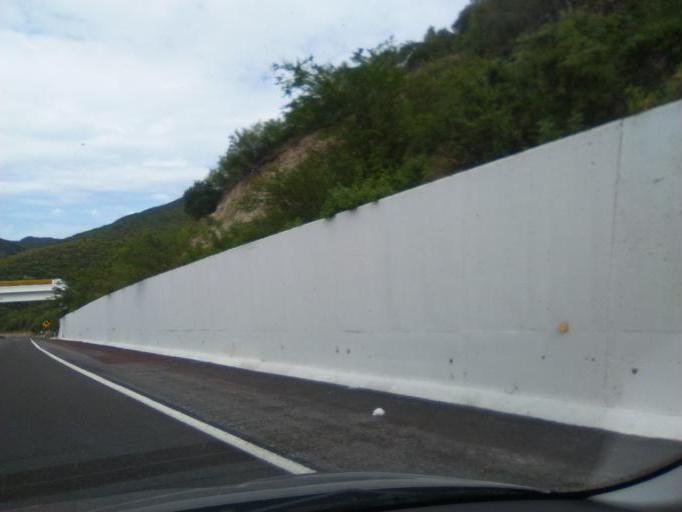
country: MX
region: Guerrero
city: Zumpango del Rio
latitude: 17.6727
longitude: -99.4956
